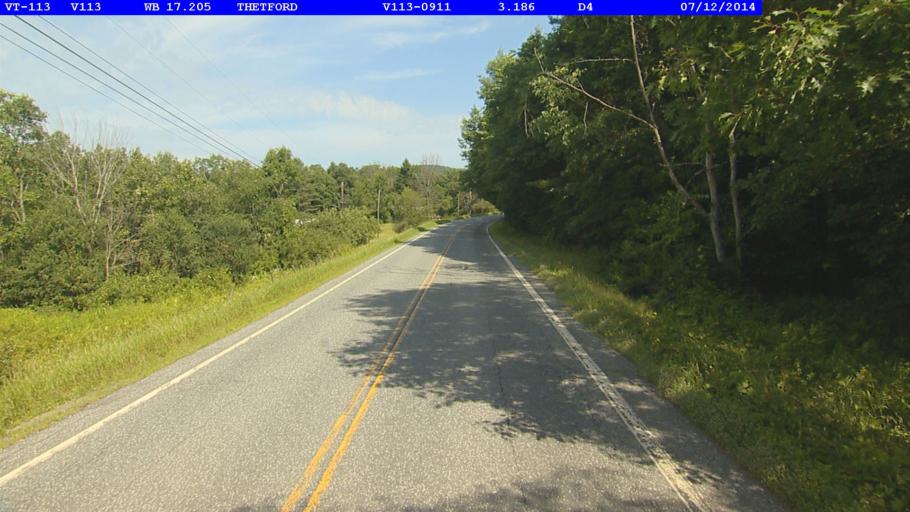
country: US
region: New Hampshire
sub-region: Grafton County
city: Lyme
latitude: 43.8531
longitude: -72.2588
